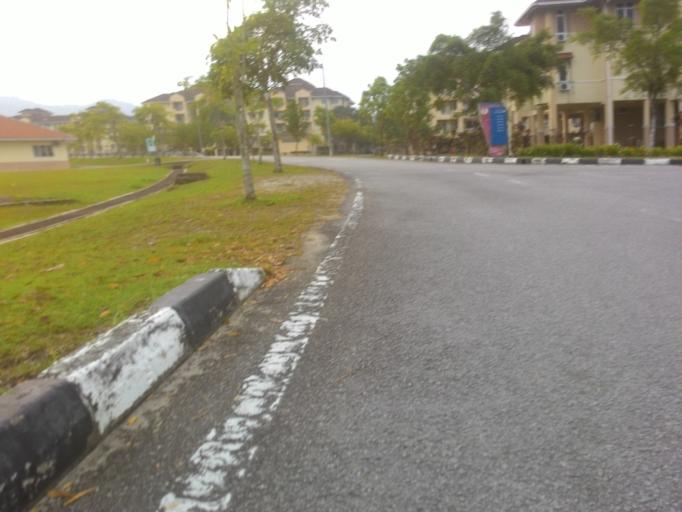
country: MY
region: Kedah
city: Kulim
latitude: 5.3807
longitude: 100.5772
